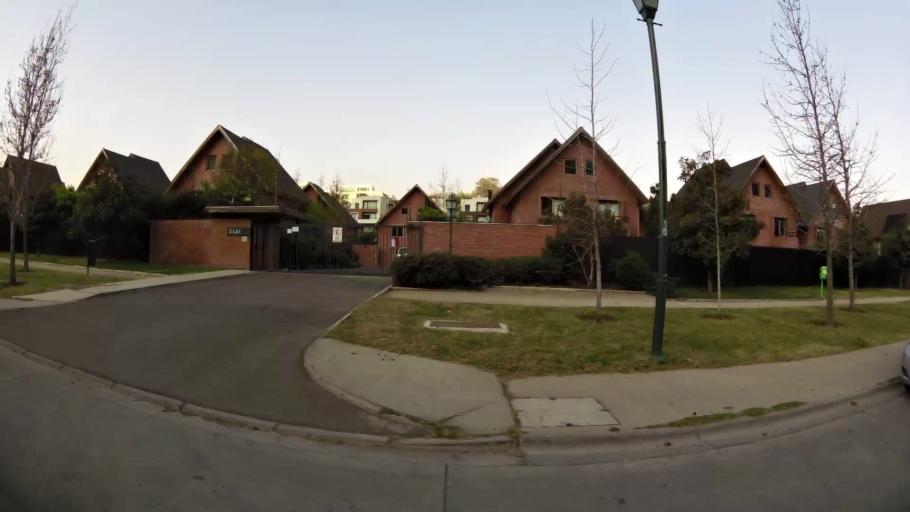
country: CL
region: Santiago Metropolitan
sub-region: Provincia de Santiago
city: Villa Presidente Frei, Nunoa, Santiago, Chile
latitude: -33.3529
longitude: -70.5456
